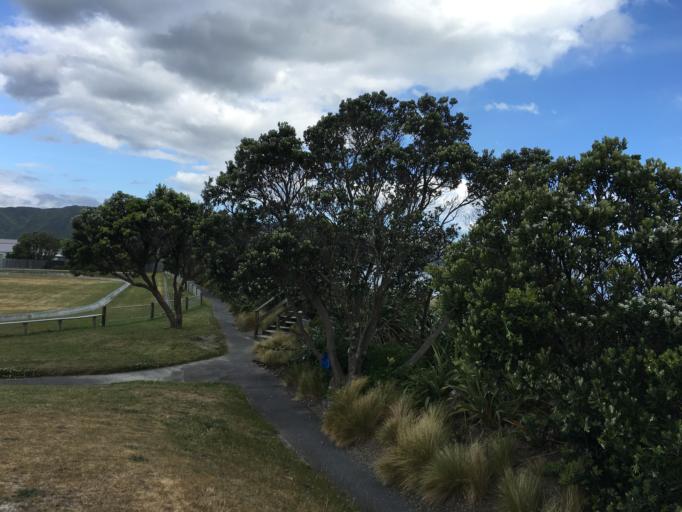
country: NZ
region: Wellington
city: Petone
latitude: -41.2322
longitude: 174.8899
